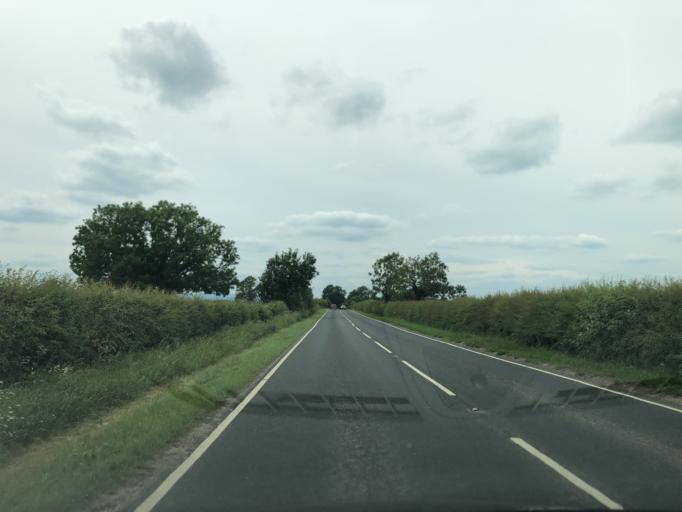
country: GB
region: England
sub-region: North Yorkshire
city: Thirsk
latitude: 54.2329
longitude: -1.3057
